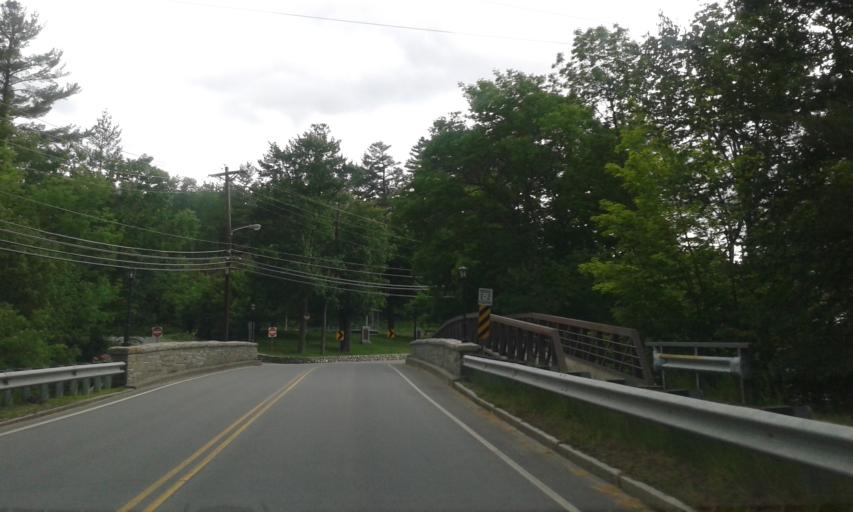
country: US
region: New Hampshire
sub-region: Grafton County
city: Woodstock
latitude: 44.0300
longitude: -71.6842
